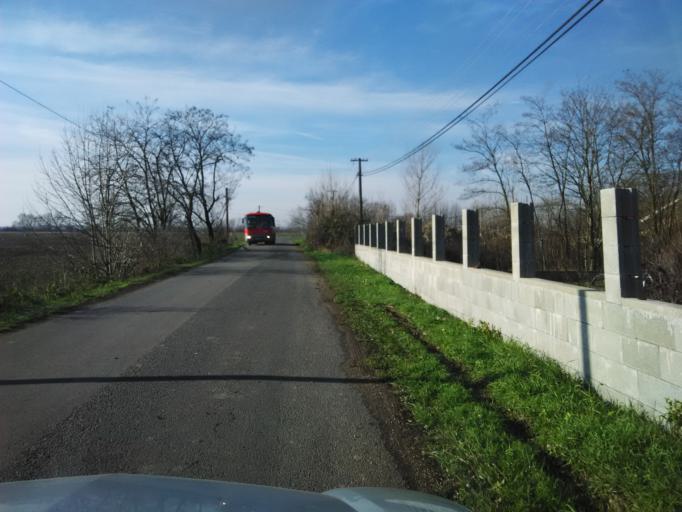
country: SK
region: Nitriansky
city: Tlmace
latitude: 48.2109
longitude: 18.5164
